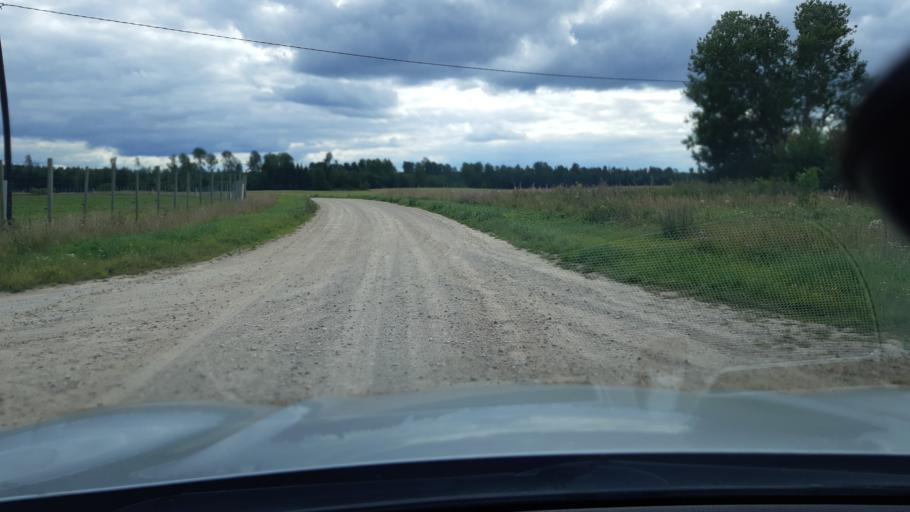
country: EE
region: Paernumaa
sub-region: Vaendra vald (alev)
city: Vandra
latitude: 58.7786
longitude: 25.0523
